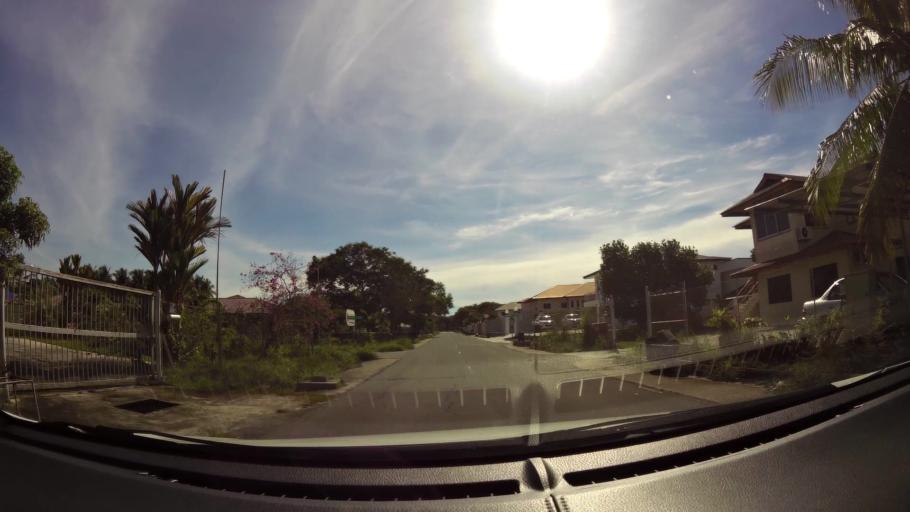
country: BN
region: Belait
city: Kuala Belait
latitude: 4.5841
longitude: 114.2047
